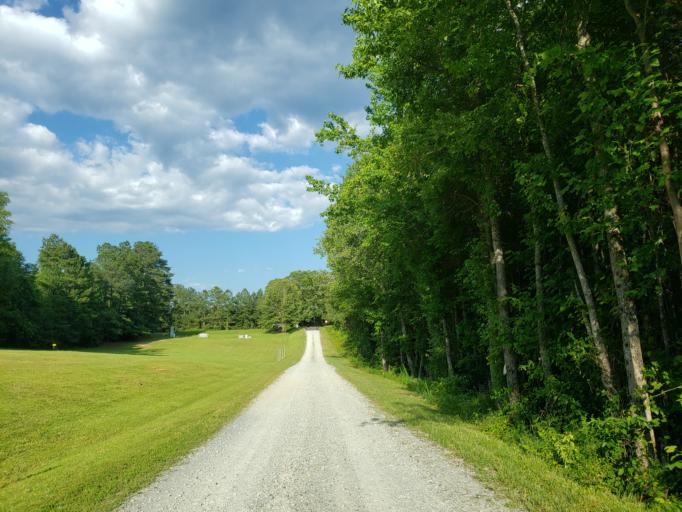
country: US
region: Georgia
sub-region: Haralson County
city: Buchanan
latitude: 33.8462
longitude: -85.2022
